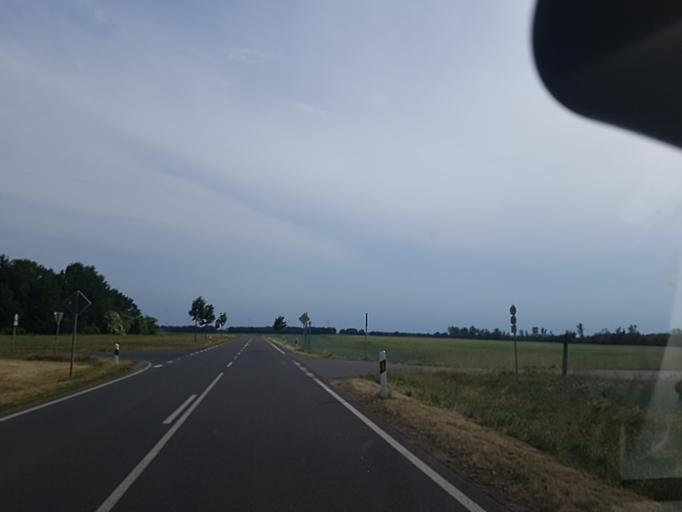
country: DE
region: Saxony-Anhalt
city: Seyda
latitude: 51.8857
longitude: 12.8949
